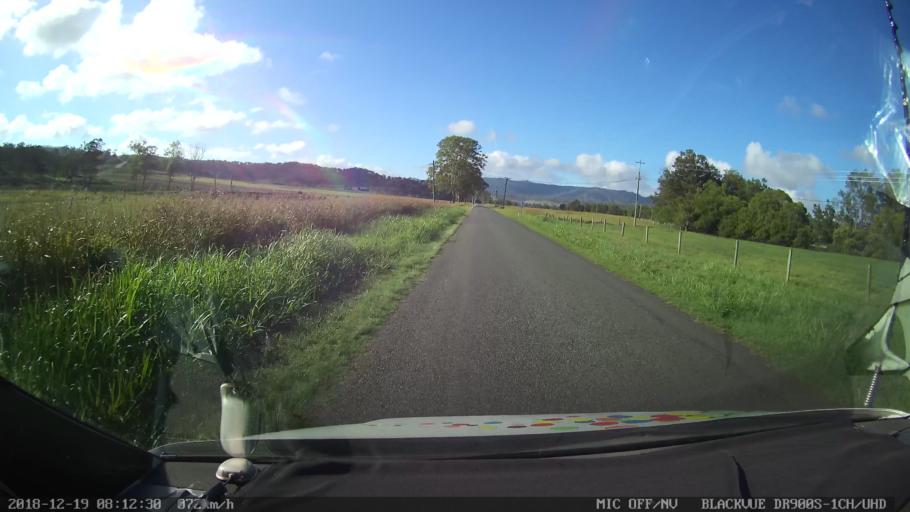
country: AU
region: Queensland
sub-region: Logan
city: Cedar Vale
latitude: -28.2279
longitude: 152.8914
